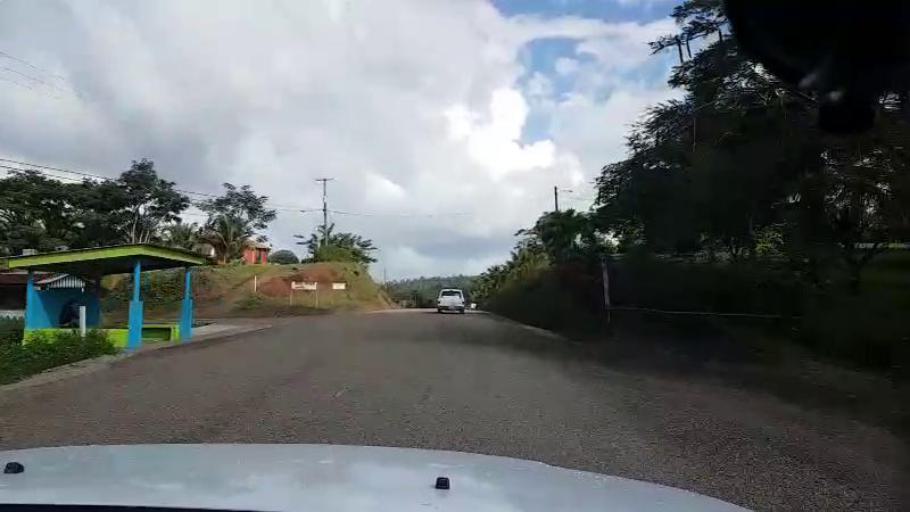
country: BZ
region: Cayo
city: Belmopan
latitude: 17.0882
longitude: -88.6144
